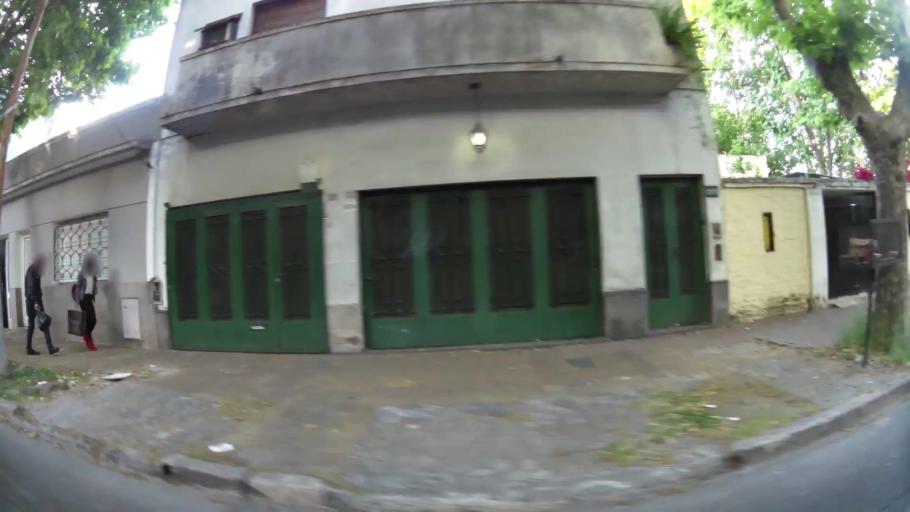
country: AR
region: Buenos Aires
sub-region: Partido de General San Martin
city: General San Martin
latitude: -34.5691
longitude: -58.5356
